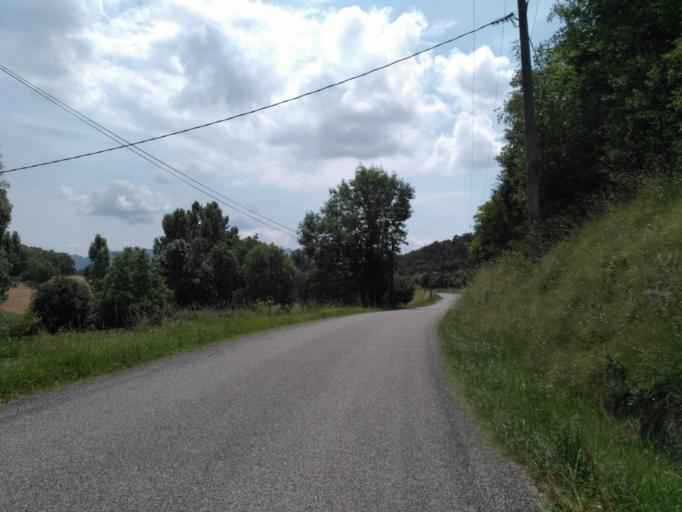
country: FR
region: Rhone-Alpes
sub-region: Departement de la Drome
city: Aouste-sur-Sye
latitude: 44.7471
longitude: 5.1126
